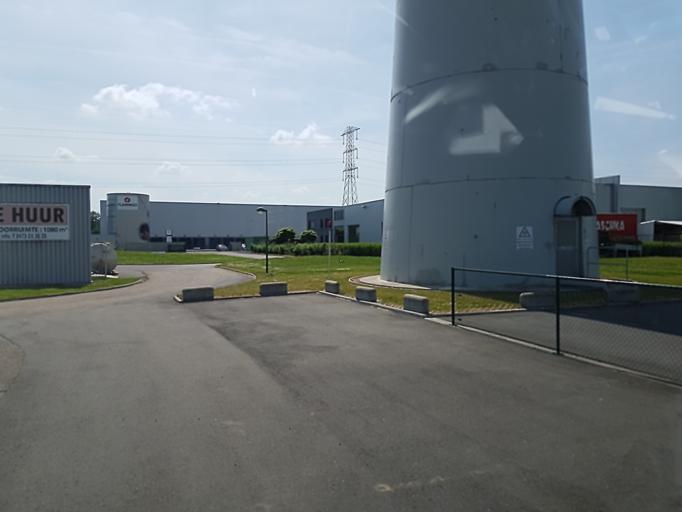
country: BE
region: Flanders
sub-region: Provincie Antwerpen
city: Westerlo
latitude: 51.1468
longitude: 4.9172
